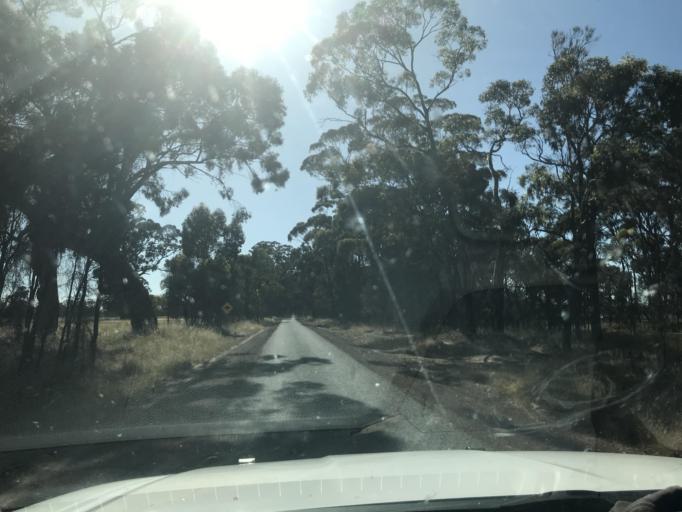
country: AU
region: Victoria
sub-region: Horsham
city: Horsham
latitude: -37.0121
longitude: 141.6685
